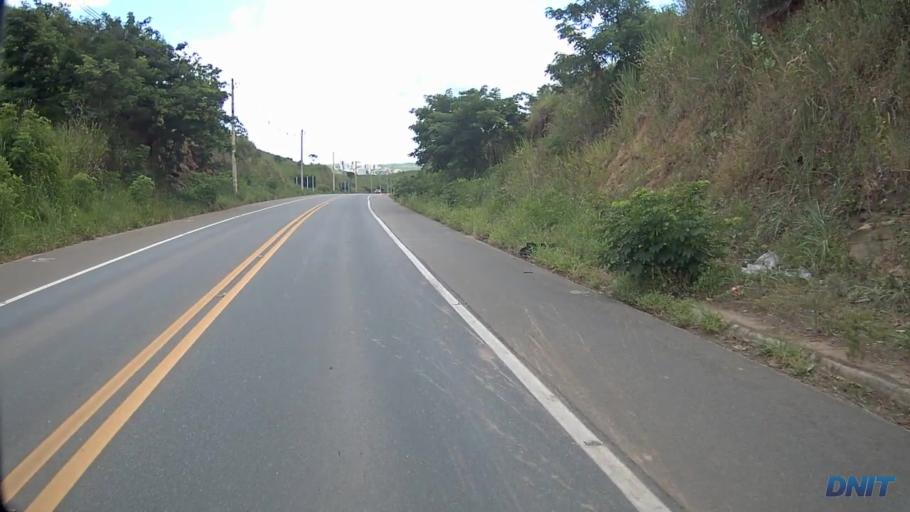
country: BR
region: Minas Gerais
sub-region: Governador Valadares
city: Governador Valadares
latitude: -18.8497
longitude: -41.9837
